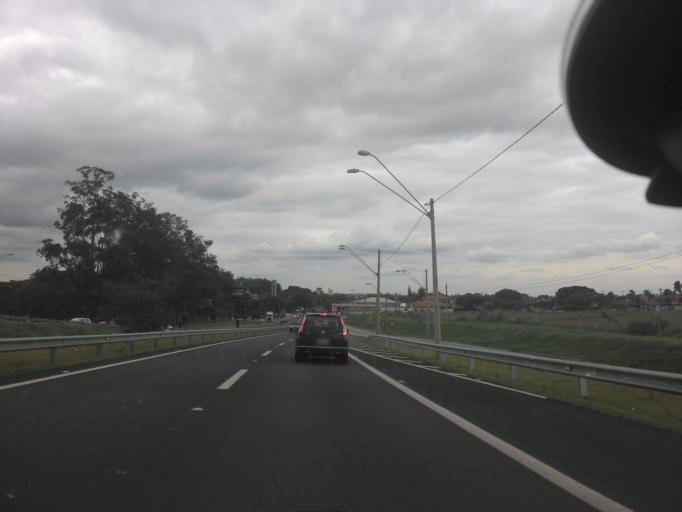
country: BR
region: Sao Paulo
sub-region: Campinas
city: Campinas
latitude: -22.8377
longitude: -47.0797
